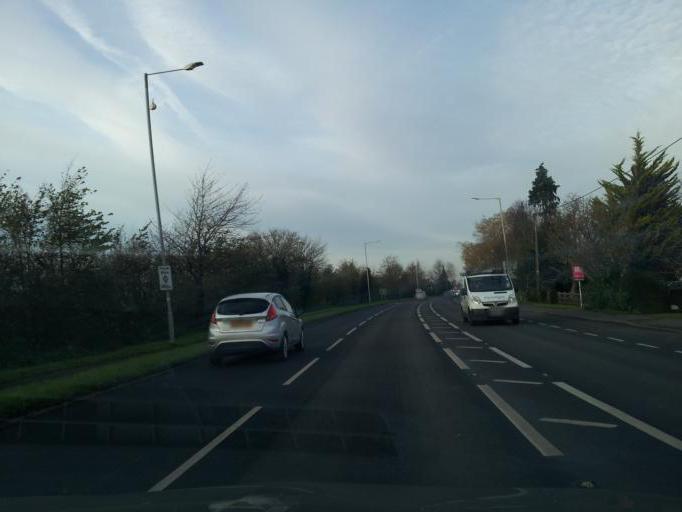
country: GB
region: England
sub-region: Buckinghamshire
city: Weston Turville
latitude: 51.7869
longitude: -0.7778
